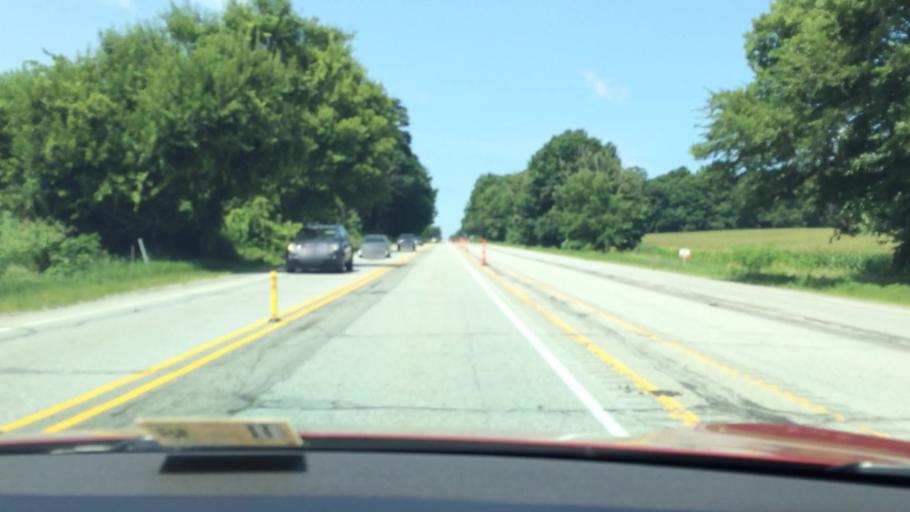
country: US
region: Indiana
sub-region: LaPorte County
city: LaPorte
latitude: 41.6739
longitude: -86.6494
